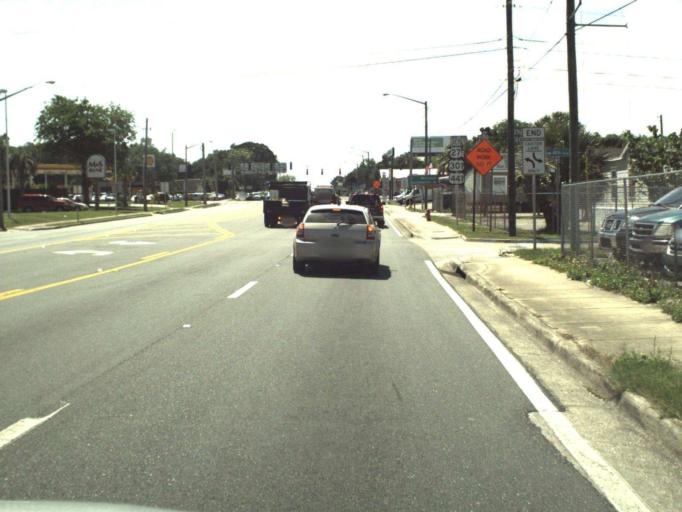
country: US
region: Florida
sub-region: Marion County
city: Ocala
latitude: 29.1970
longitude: -82.1401
